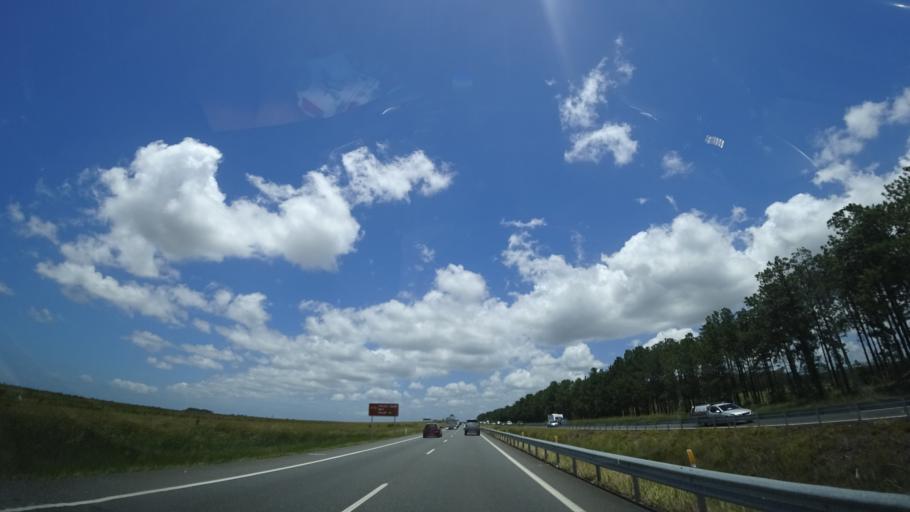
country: AU
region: Queensland
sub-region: Sunshine Coast
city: Little Mountain
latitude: -26.8170
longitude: 153.0371
